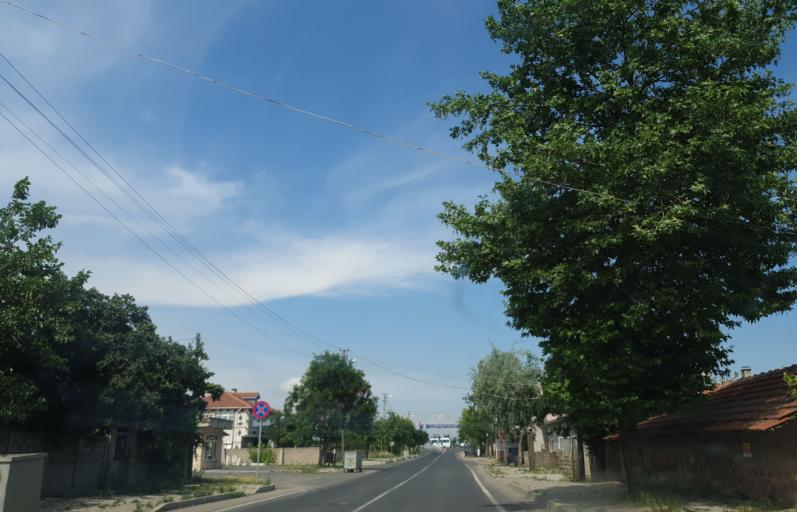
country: TR
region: Tekirdag
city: Beyazkoy
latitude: 41.2638
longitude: 27.6502
